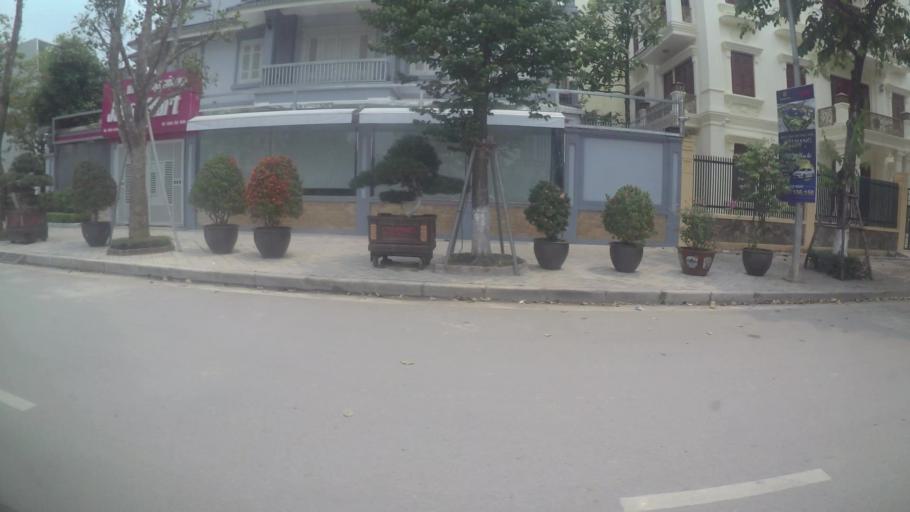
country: VN
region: Ha Noi
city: Ha Dong
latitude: 20.9774
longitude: 105.7599
